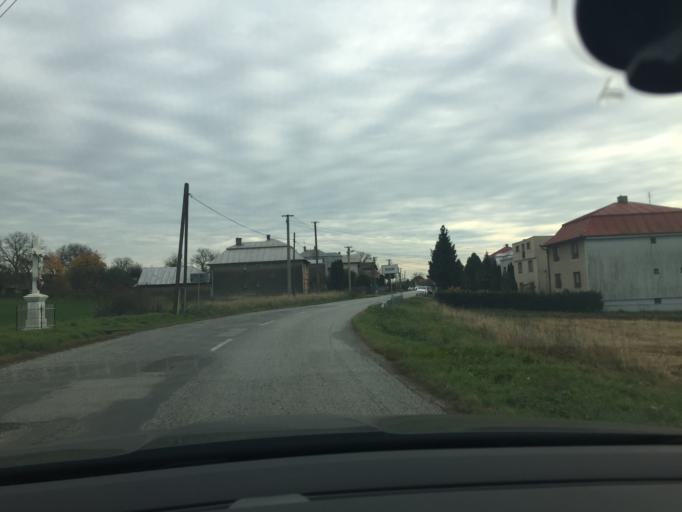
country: SK
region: Kosicky
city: Kosice
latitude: 48.8194
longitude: 21.3249
